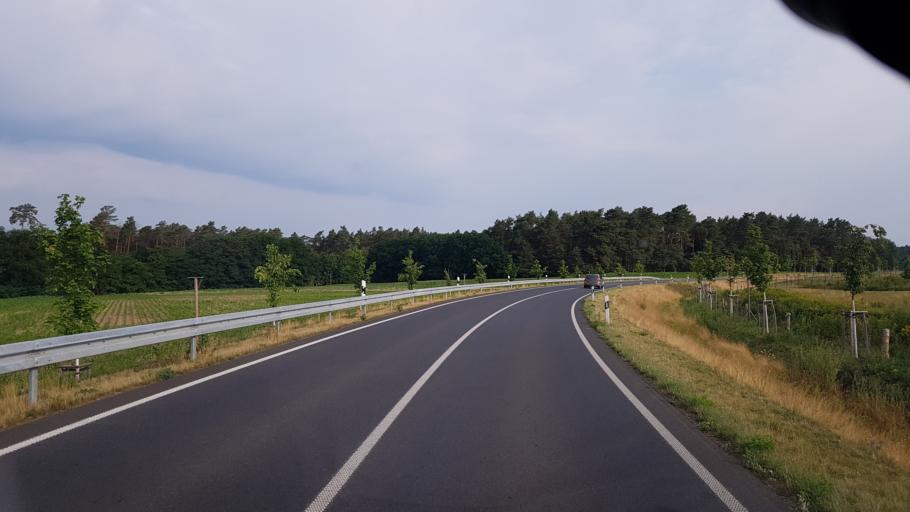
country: DE
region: Brandenburg
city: Golssen
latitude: 51.9805
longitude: 13.5629
